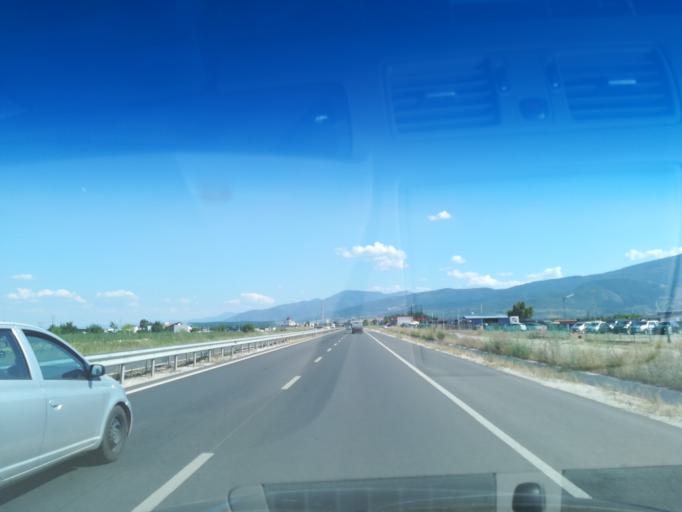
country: BG
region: Plovdiv
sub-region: Obshtina Plovdiv
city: Plovdiv
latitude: 42.0866
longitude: 24.7964
